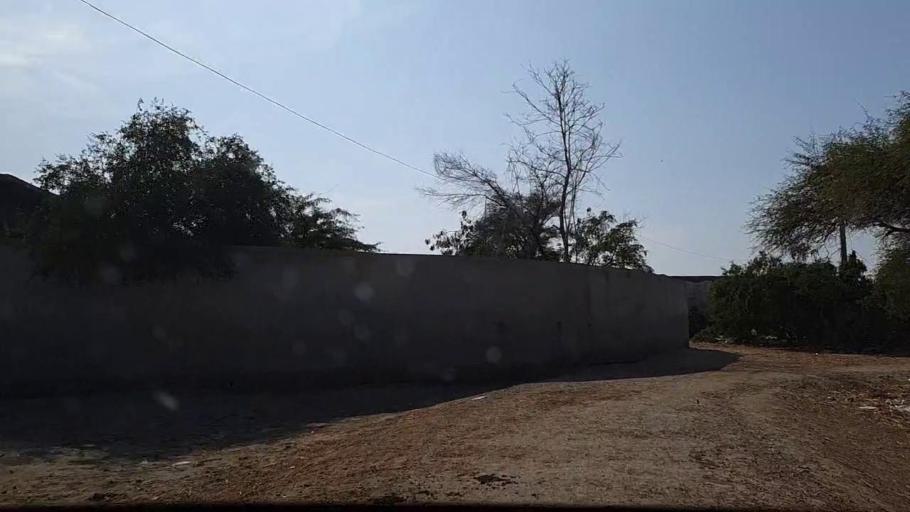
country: PK
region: Sindh
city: Daro Mehar
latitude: 24.7221
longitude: 68.1539
